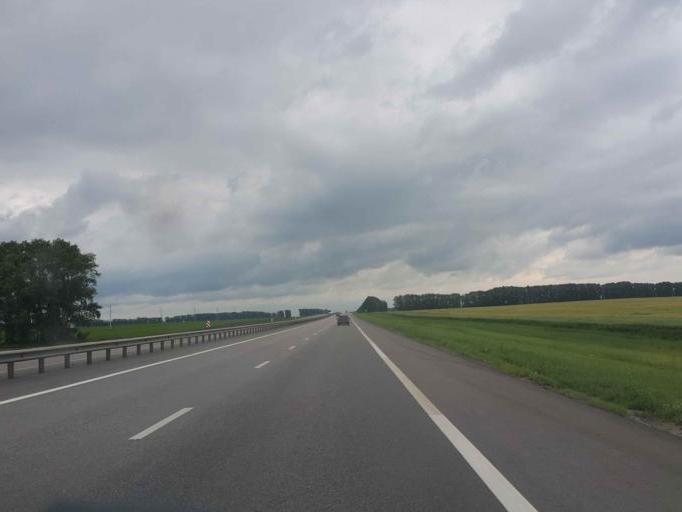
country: RU
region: Tambov
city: Zavoronezhskoye
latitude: 52.8381
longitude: 40.8548
